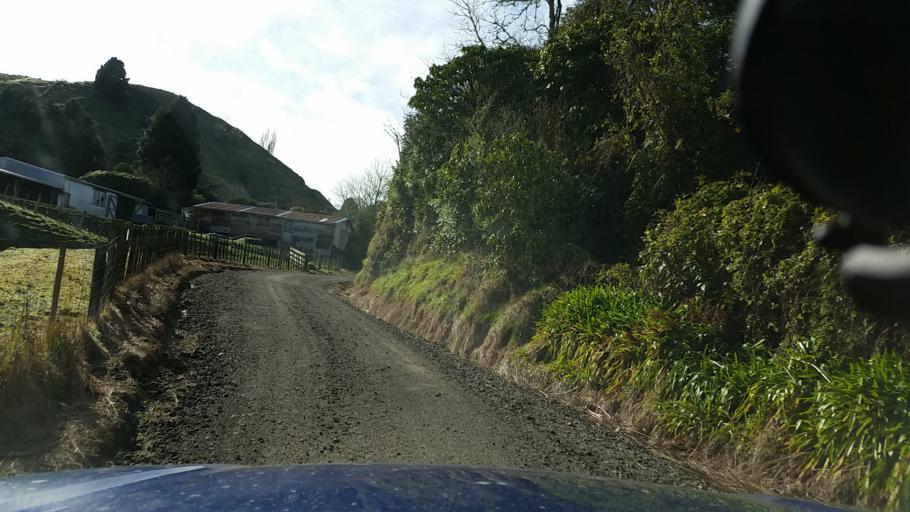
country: NZ
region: Taranaki
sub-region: New Plymouth District
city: Waitara
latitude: -39.0346
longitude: 174.7831
